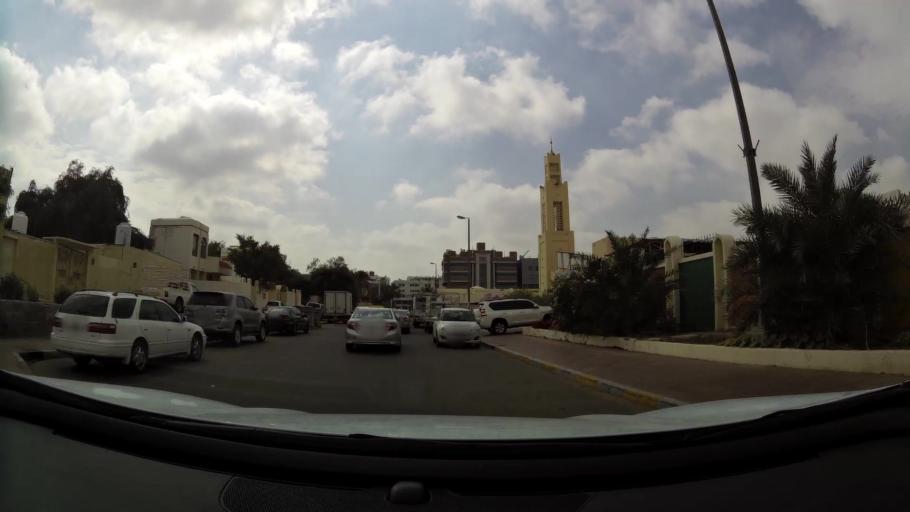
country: AE
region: Abu Dhabi
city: Al Ain
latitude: 24.2294
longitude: 55.7592
